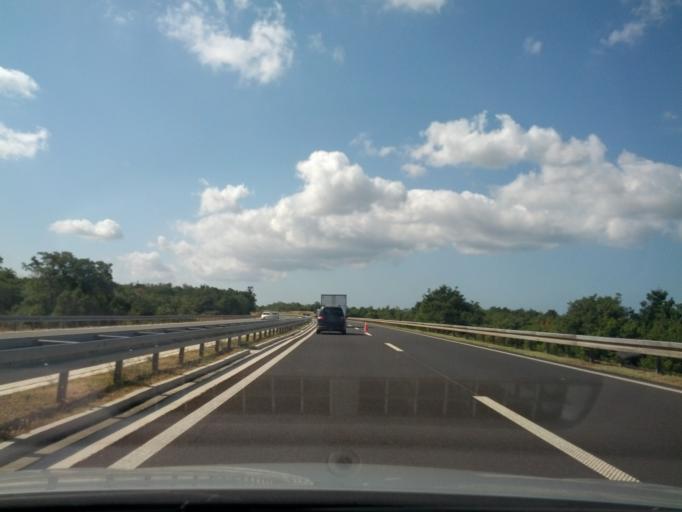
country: HR
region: Istarska
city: Vodnjan
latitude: 45.0059
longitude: 13.8372
